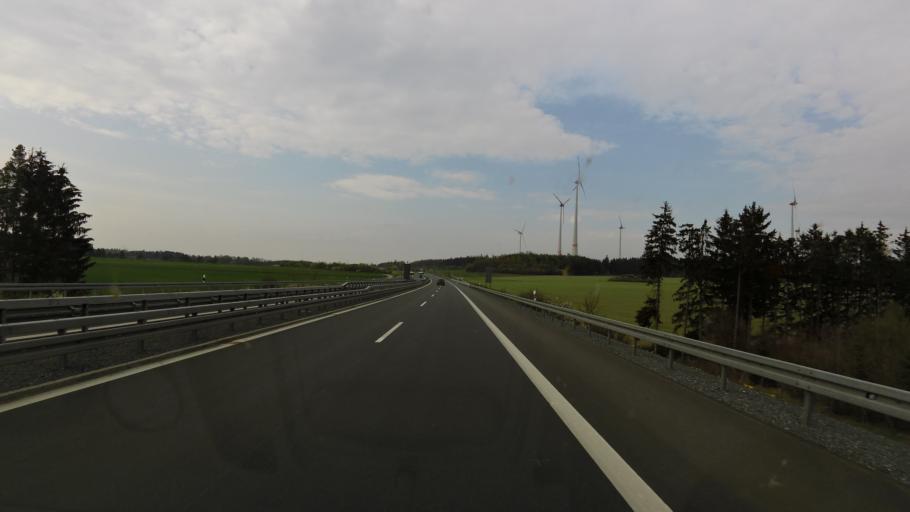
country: DE
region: Bavaria
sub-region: Upper Franconia
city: Gattendorf
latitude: 50.3174
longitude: 12.0236
